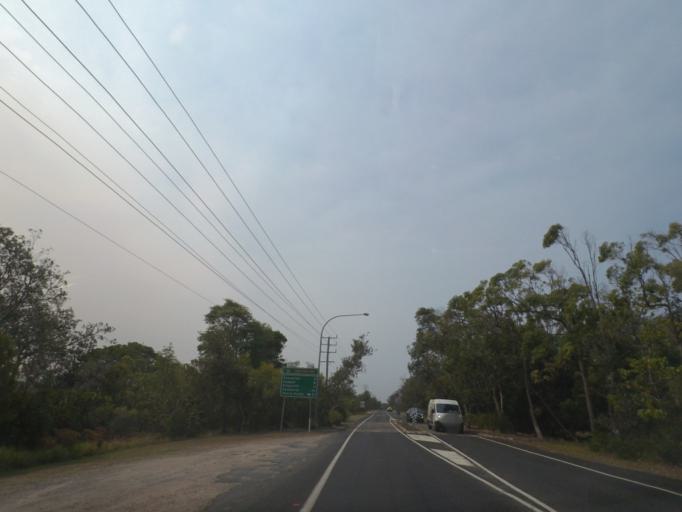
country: AU
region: New South Wales
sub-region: Tweed
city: Casuarina
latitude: -28.3278
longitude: 153.5685
